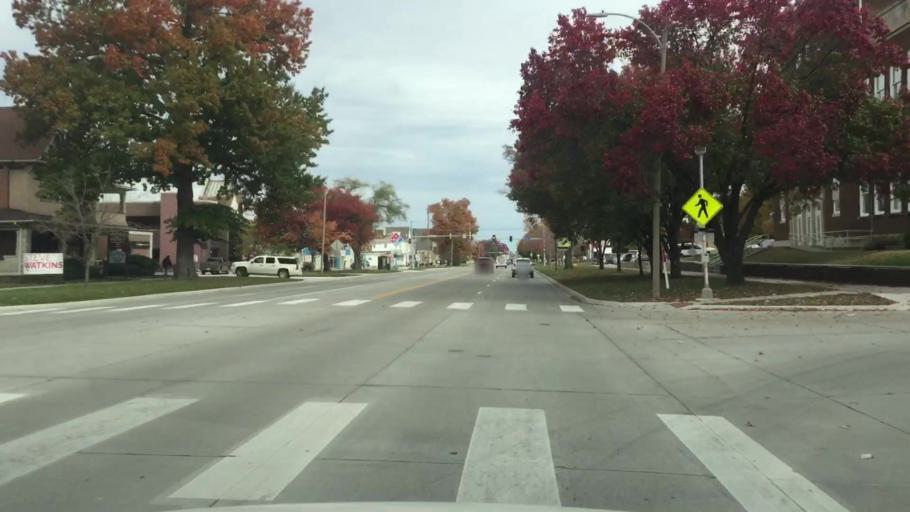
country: US
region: Kansas
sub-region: Shawnee County
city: Topeka
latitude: 39.0488
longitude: -95.6809
